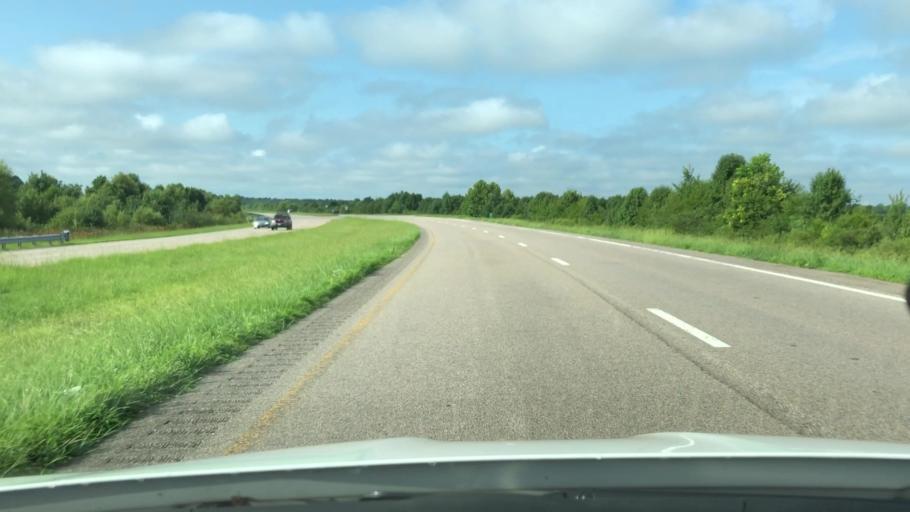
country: US
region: Virginia
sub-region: City of Portsmouth
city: Portsmouth Heights
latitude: 36.7028
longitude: -76.3430
